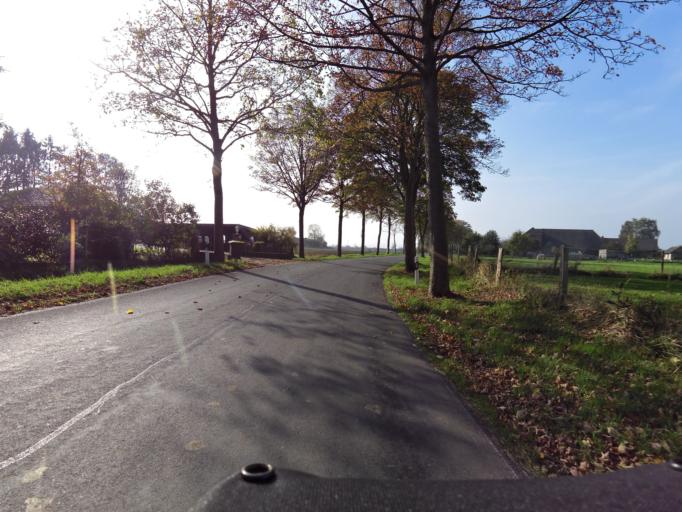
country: DE
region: North Rhine-Westphalia
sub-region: Regierungsbezirk Dusseldorf
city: Kranenburg
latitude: 51.8256
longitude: 6.0181
